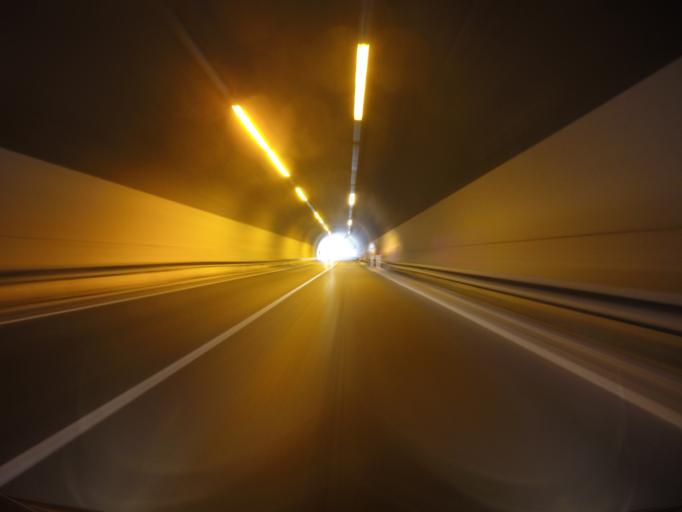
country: IT
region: Sicily
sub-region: Palermo
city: Agliandroni-Paternella
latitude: 38.1239
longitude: 13.0761
